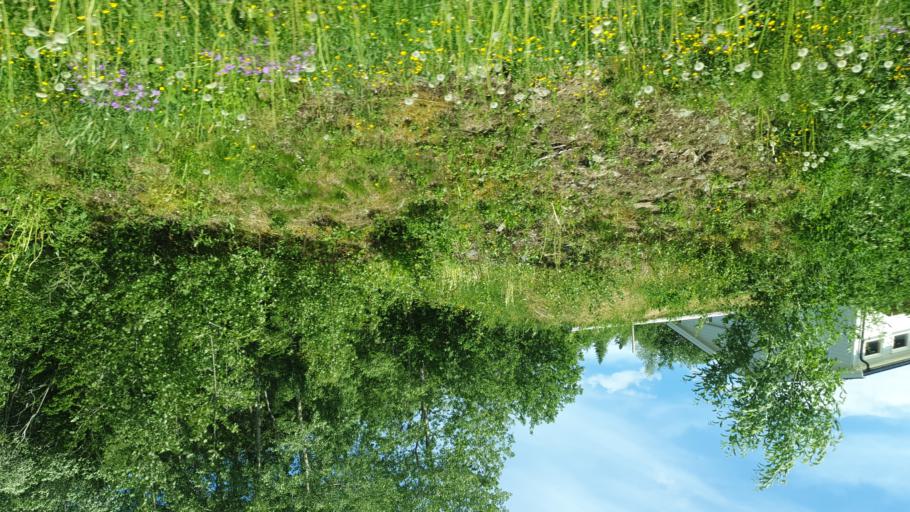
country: NO
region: Nord-Trondelag
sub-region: Leksvik
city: Leksvik
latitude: 63.6909
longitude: 10.6773
